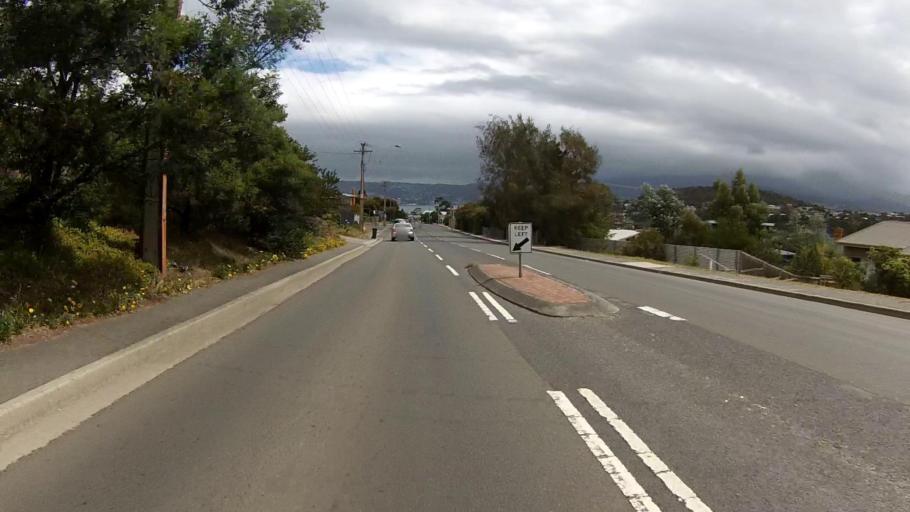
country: AU
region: Tasmania
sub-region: Clarence
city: Bellerive
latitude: -42.8648
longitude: 147.3749
